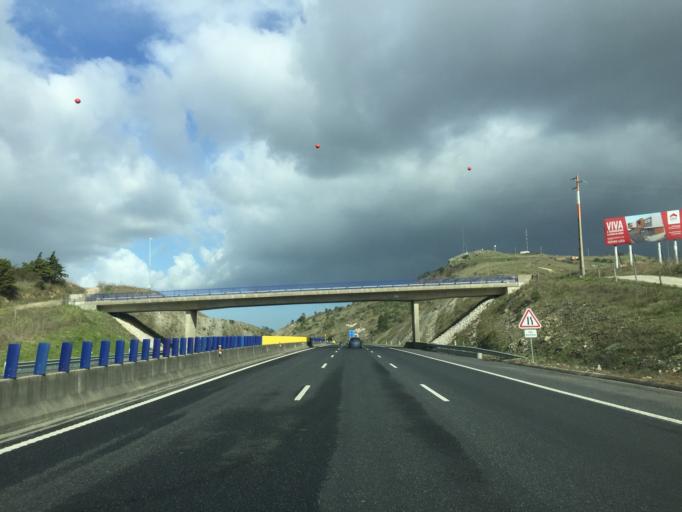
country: PT
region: Lisbon
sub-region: Mafra
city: Venda do Pinheiro
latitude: 38.8899
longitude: -9.1957
